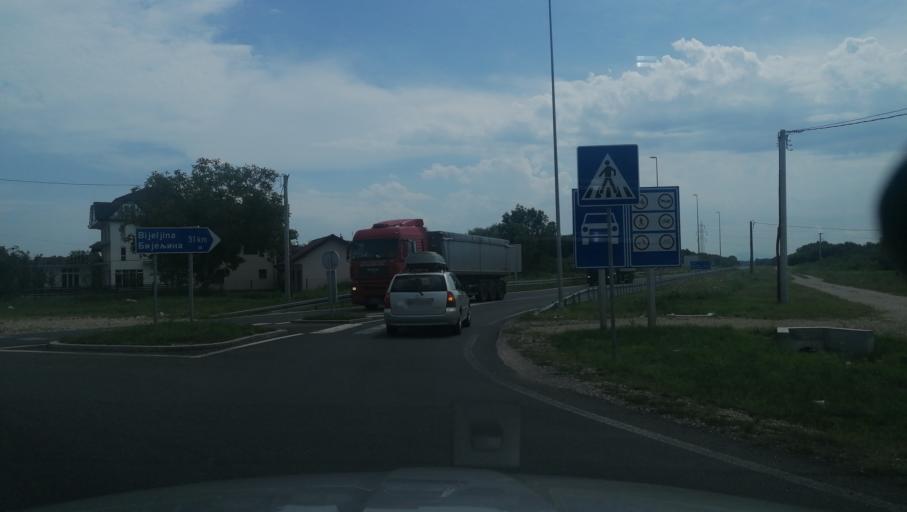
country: BA
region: Brcko
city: Brcko
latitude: 44.9144
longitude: 18.7415
